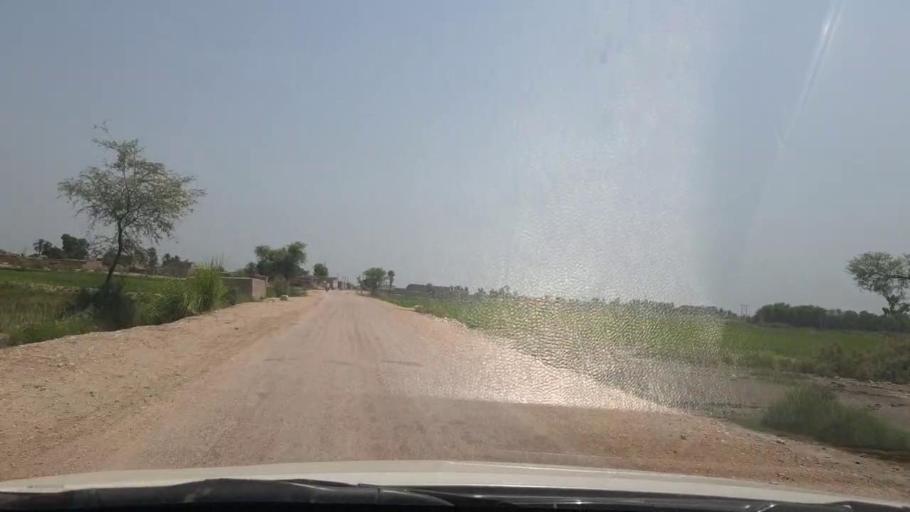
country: PK
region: Sindh
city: Rustam jo Goth
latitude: 28.0277
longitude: 68.7990
